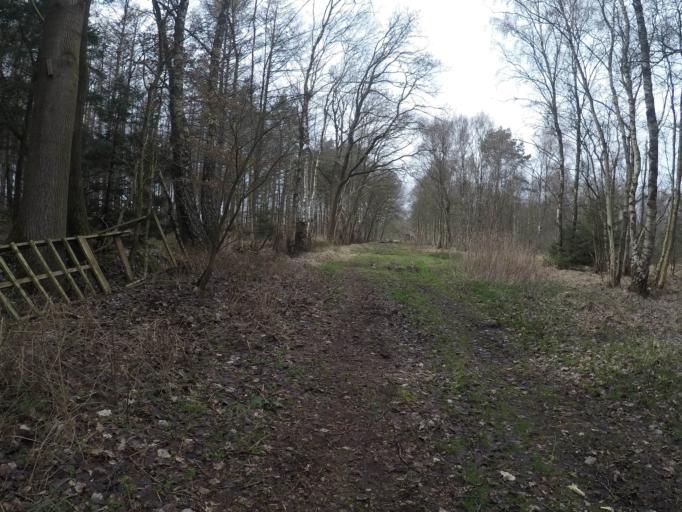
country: DE
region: Lower Saxony
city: Elmlohe
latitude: 53.6231
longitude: 8.6809
